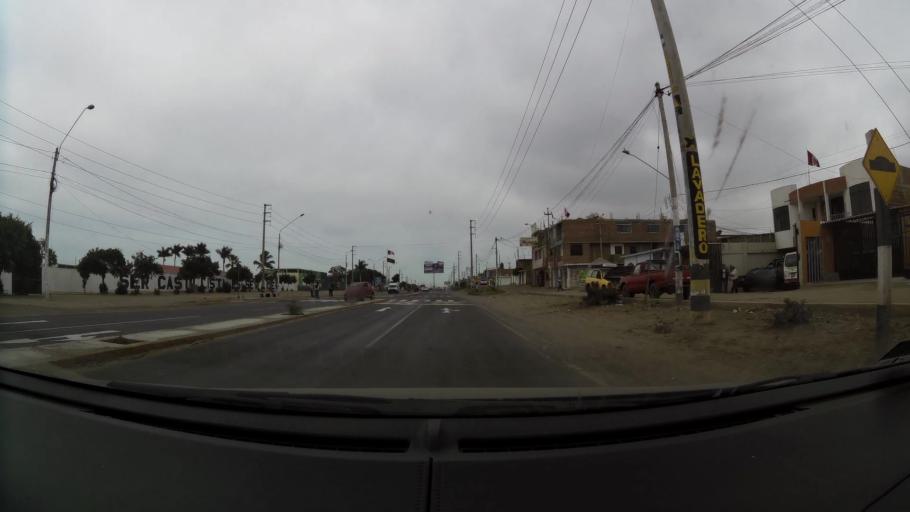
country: PE
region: La Libertad
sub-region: Provincia de Trujillo
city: Huanchaco
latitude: -8.0916
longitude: -79.0831
